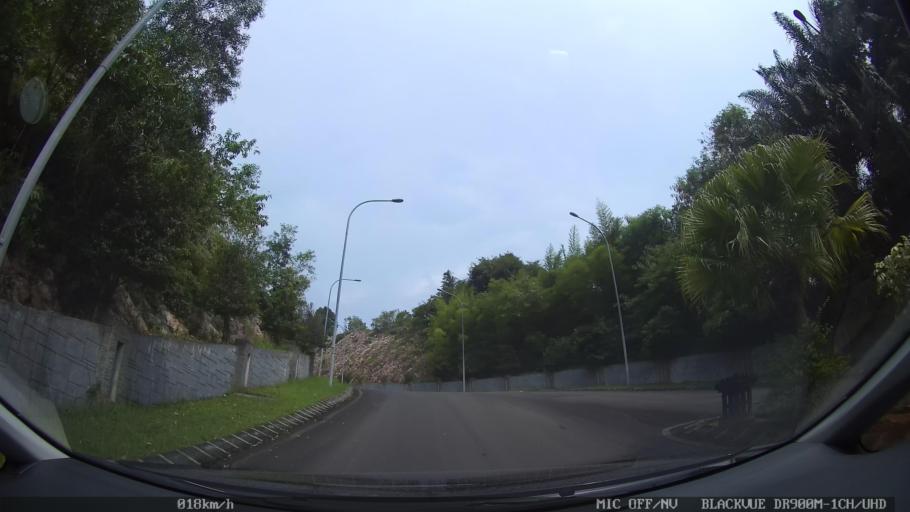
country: ID
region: Lampung
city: Bandarlampung
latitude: -5.4296
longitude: 105.2792
